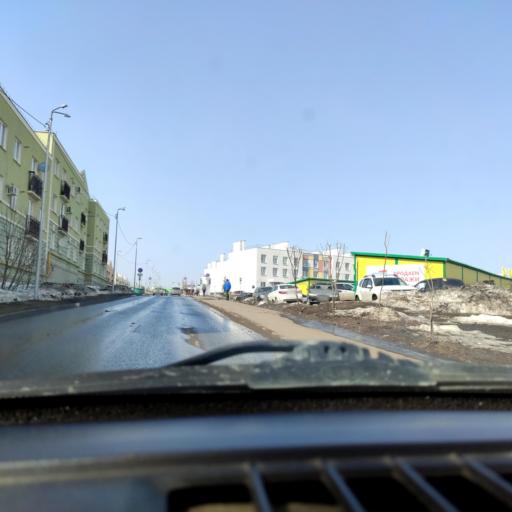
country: RU
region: Samara
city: Petra-Dubrava
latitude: 53.3196
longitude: 50.3148
